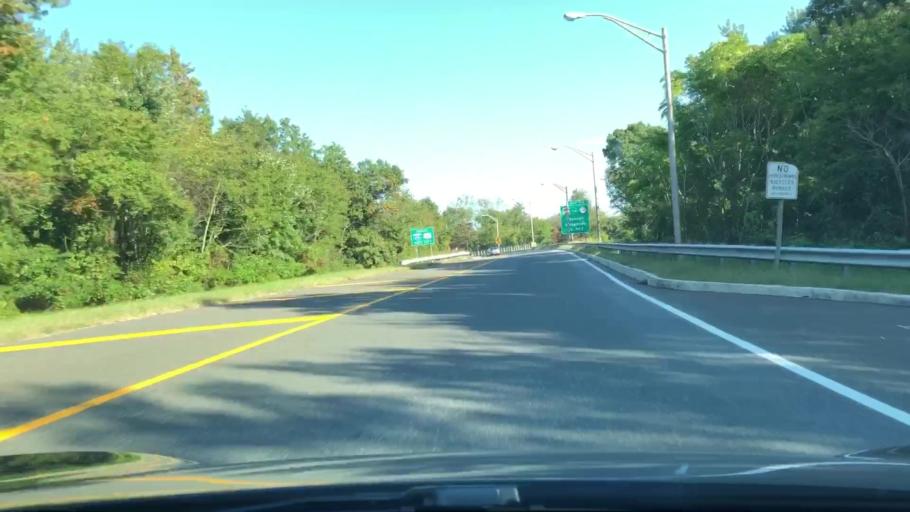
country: US
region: New Jersey
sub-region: Gloucester County
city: Gibbstown
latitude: 39.8032
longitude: -75.3148
